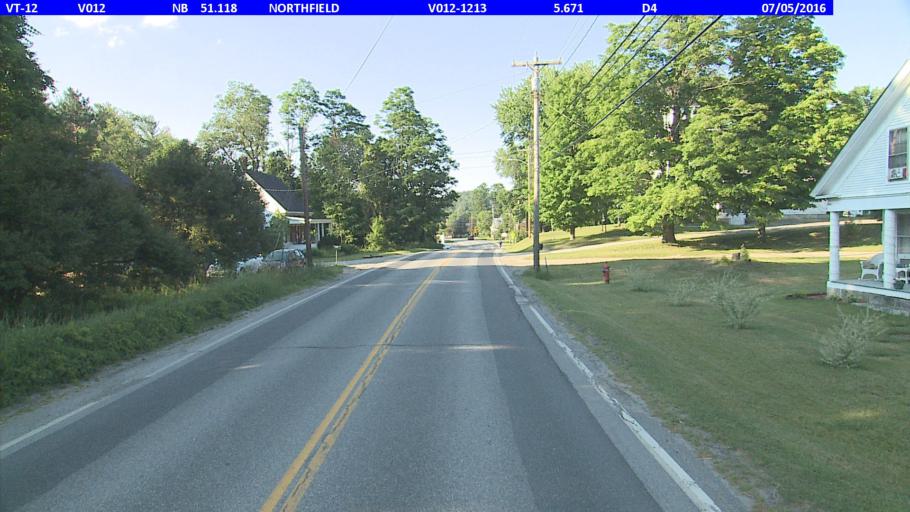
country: US
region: Vermont
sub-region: Washington County
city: Northfield
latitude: 44.1693
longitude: -72.6524
